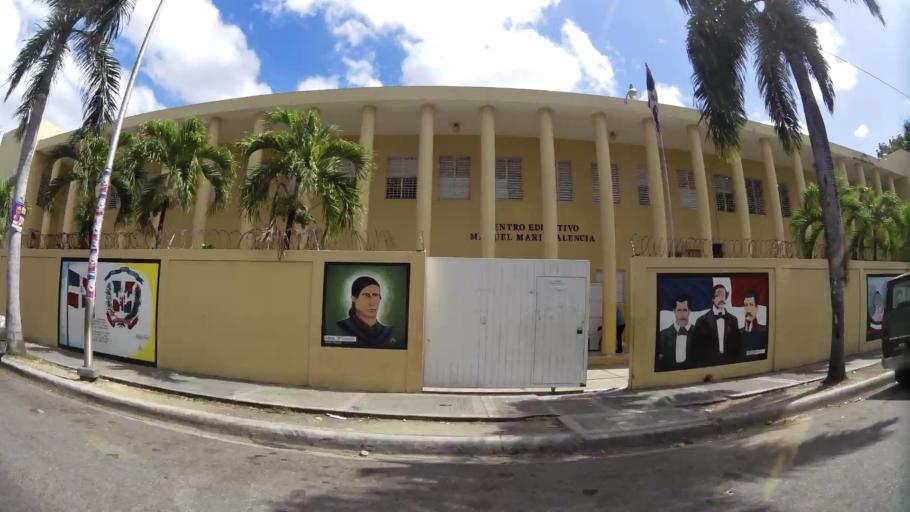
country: DO
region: San Cristobal
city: San Cristobal
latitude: 18.4189
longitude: -70.1127
